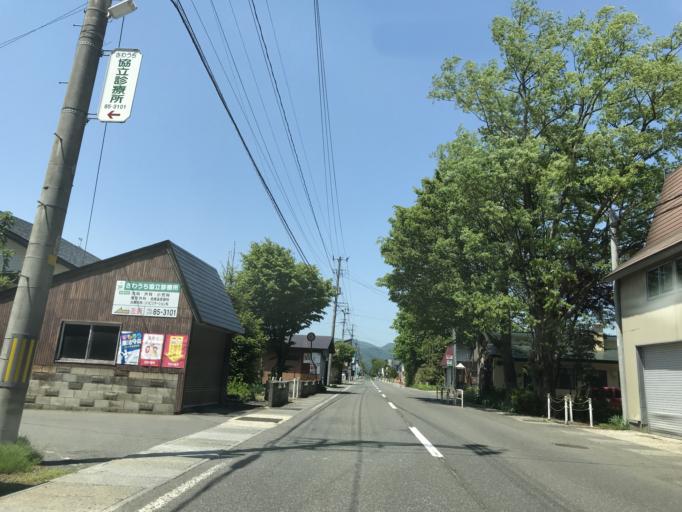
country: JP
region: Akita
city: Yokotemachi
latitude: 39.3951
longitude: 140.7577
